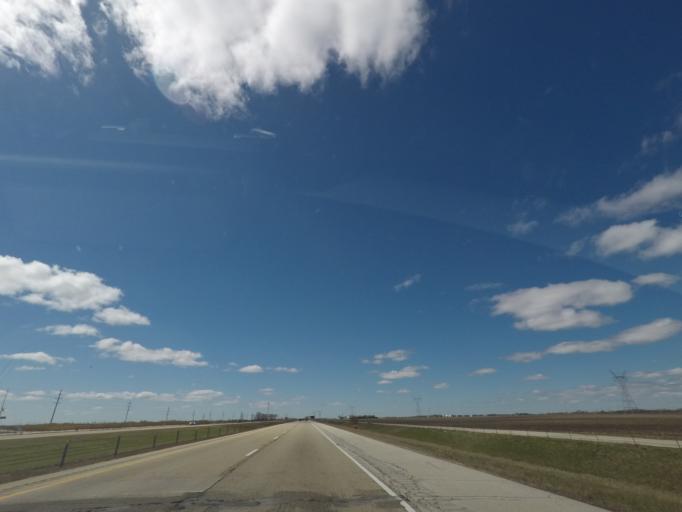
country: US
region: Illinois
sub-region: Grundy County
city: Gardner
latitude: 41.1498
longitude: -88.3574
